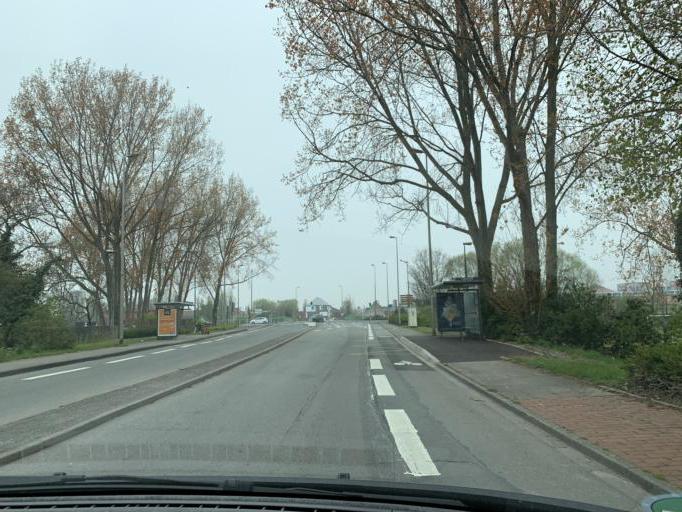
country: FR
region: Nord-Pas-de-Calais
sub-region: Departement du Nord
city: Dunkerque
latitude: 51.0257
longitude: 2.3603
